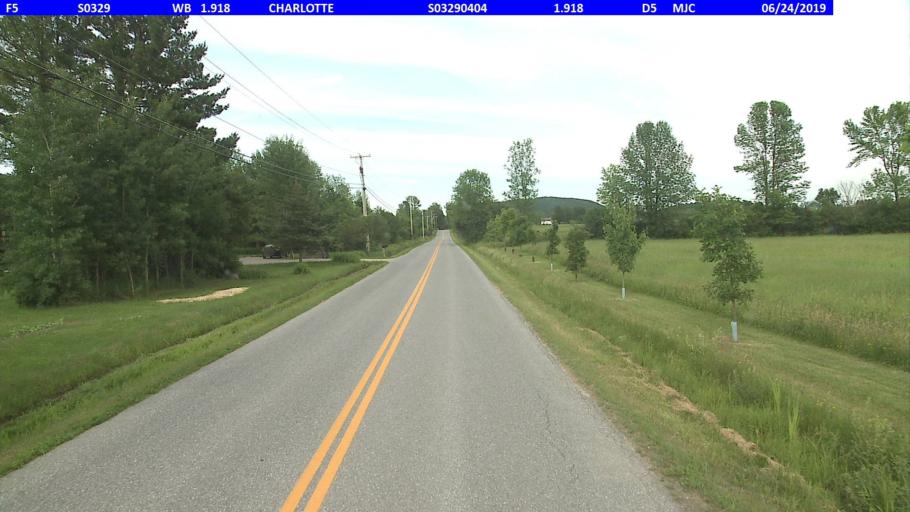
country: US
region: Vermont
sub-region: Addison County
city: Vergennes
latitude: 44.3071
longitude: -73.2840
